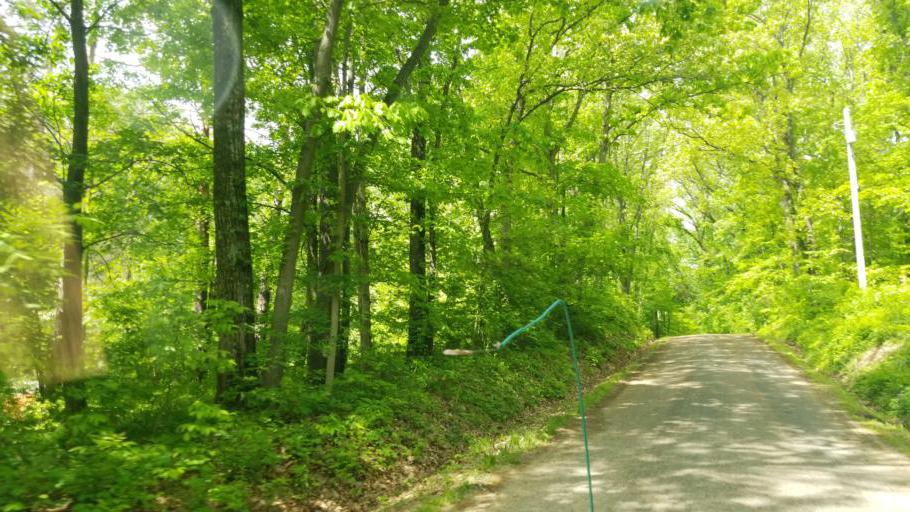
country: US
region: Ohio
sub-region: Ashland County
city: Ashland
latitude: 40.8095
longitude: -82.3813
